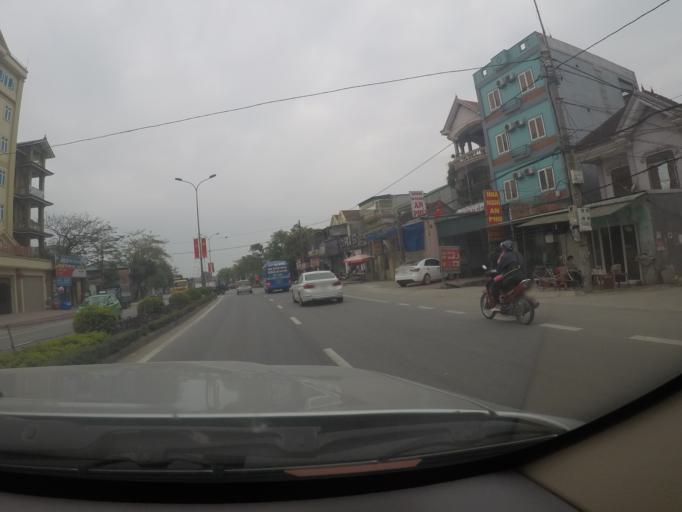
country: VN
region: Nghe An
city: Dien Chau
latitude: 18.9711
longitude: 105.6008
